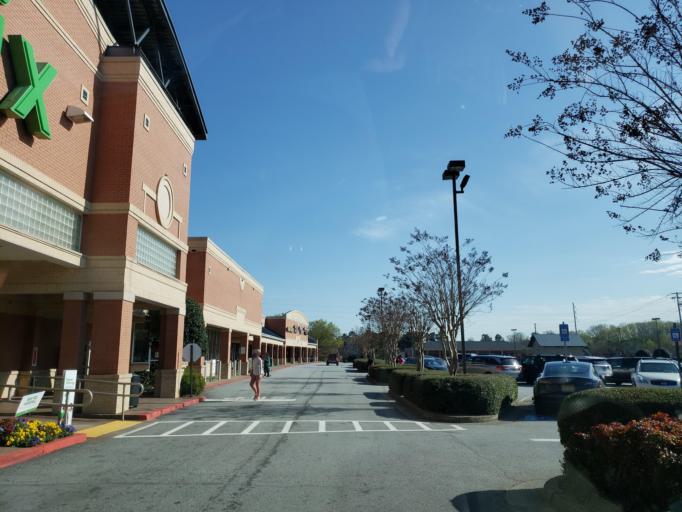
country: US
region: Georgia
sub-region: Cobb County
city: Marietta
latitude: 33.9764
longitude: -84.4788
